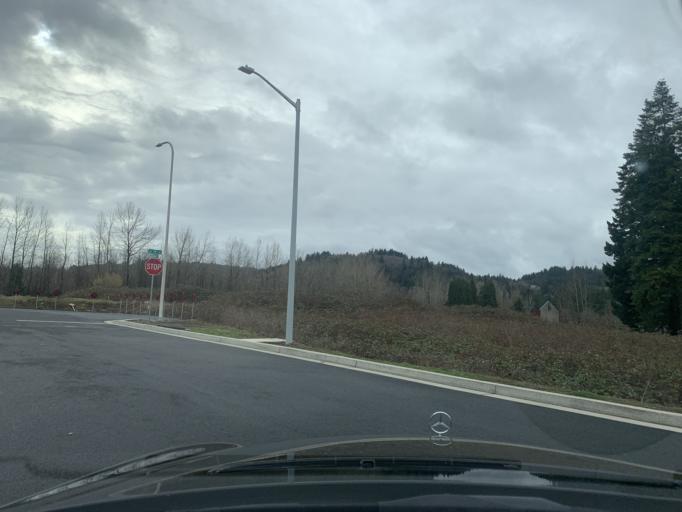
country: US
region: Oregon
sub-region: Multnomah County
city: Gresham
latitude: 45.4836
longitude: -122.4109
